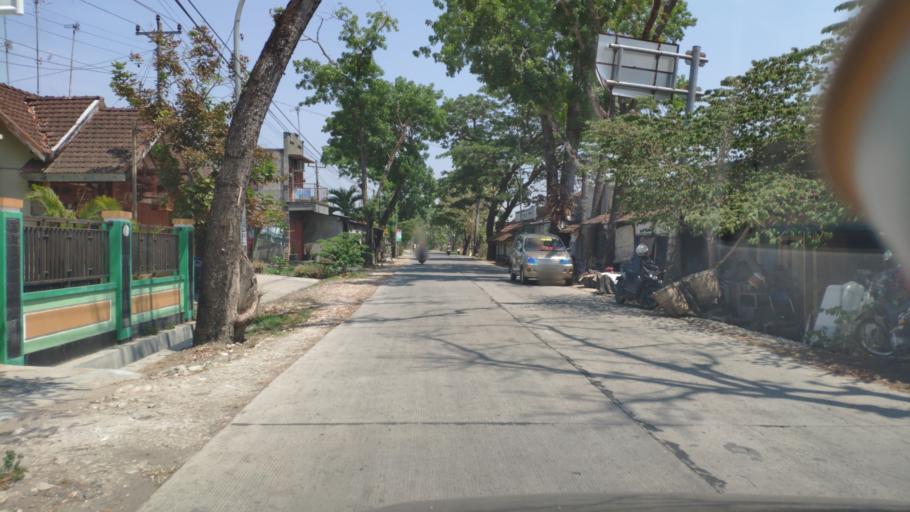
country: ID
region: Central Java
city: Jagong
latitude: -7.0499
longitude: 111.2256
